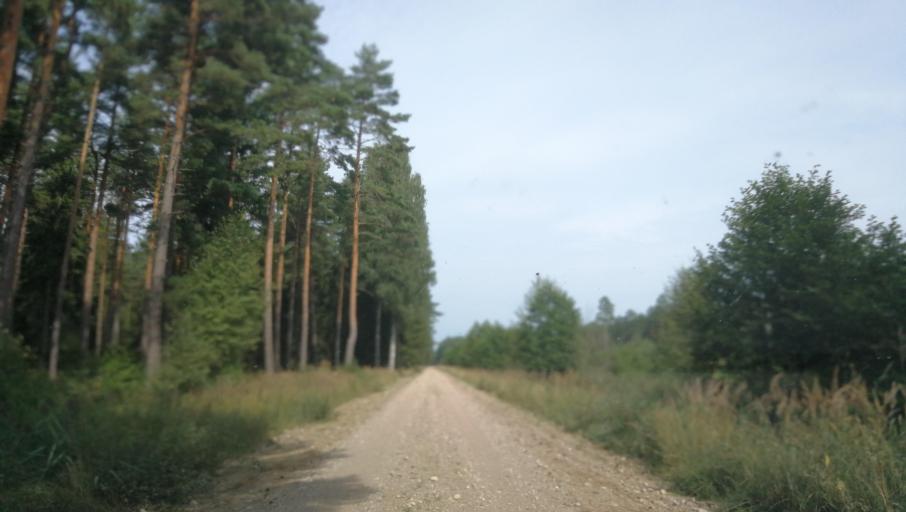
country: LV
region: Pavilostas
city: Pavilosta
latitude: 56.8219
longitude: 21.2886
